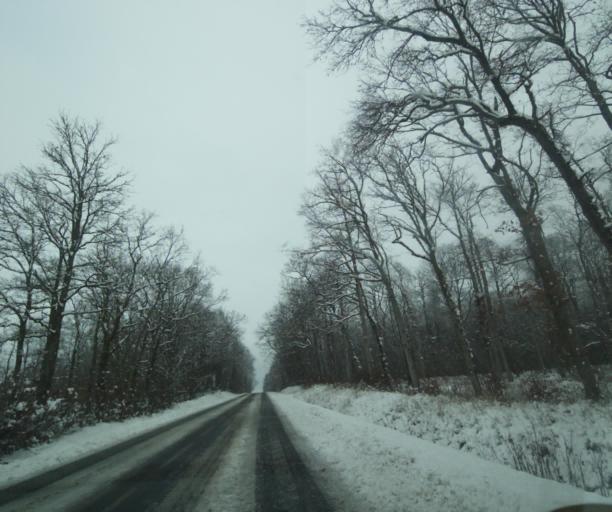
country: FR
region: Champagne-Ardenne
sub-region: Departement de la Haute-Marne
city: Montier-en-Der
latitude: 48.5260
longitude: 4.7486
